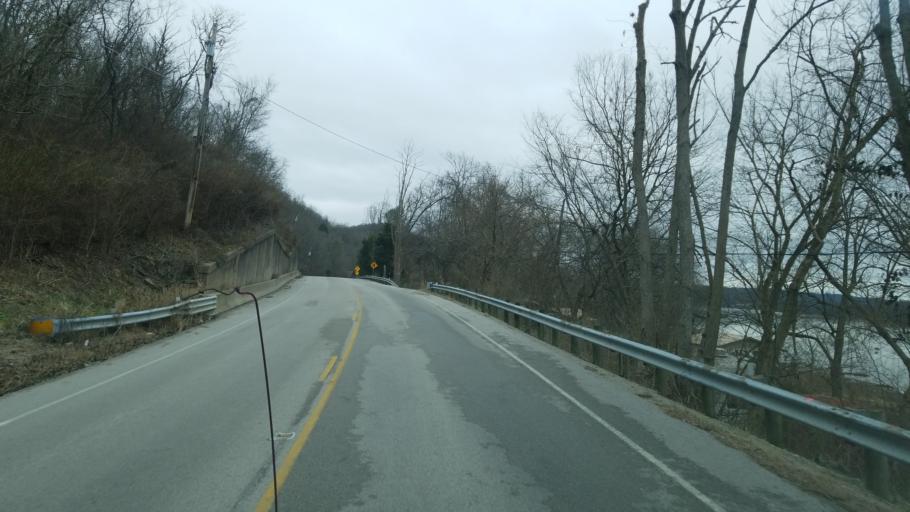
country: US
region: Ohio
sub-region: Brown County
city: Ripley
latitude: 38.7667
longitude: -83.8872
